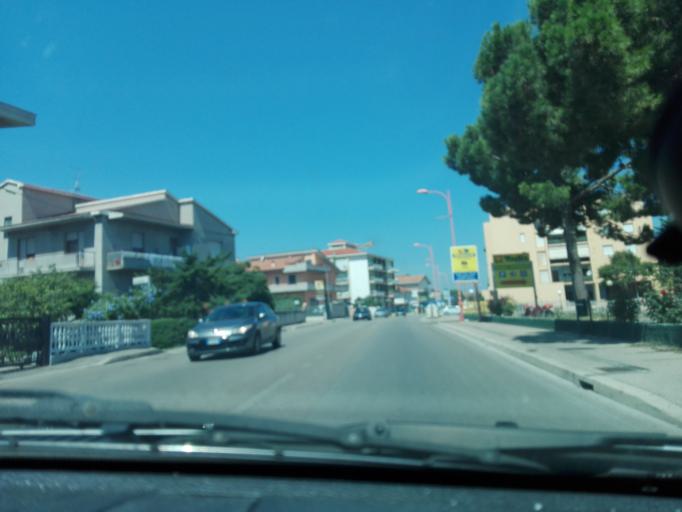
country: IT
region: Abruzzo
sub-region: Provincia di Pescara
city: Montesilvano Marina
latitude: 42.5060
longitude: 14.1597
